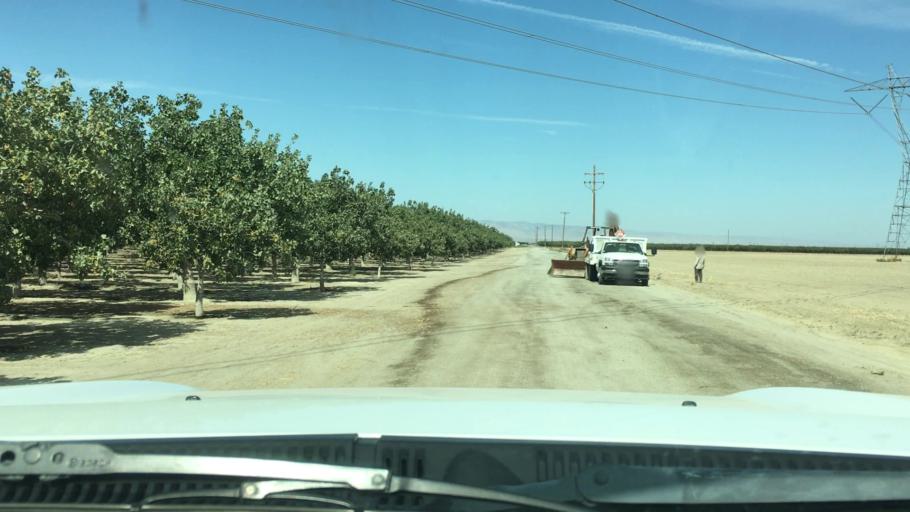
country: US
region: California
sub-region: Kern County
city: Buttonwillow
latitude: 35.3766
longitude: -119.3986
